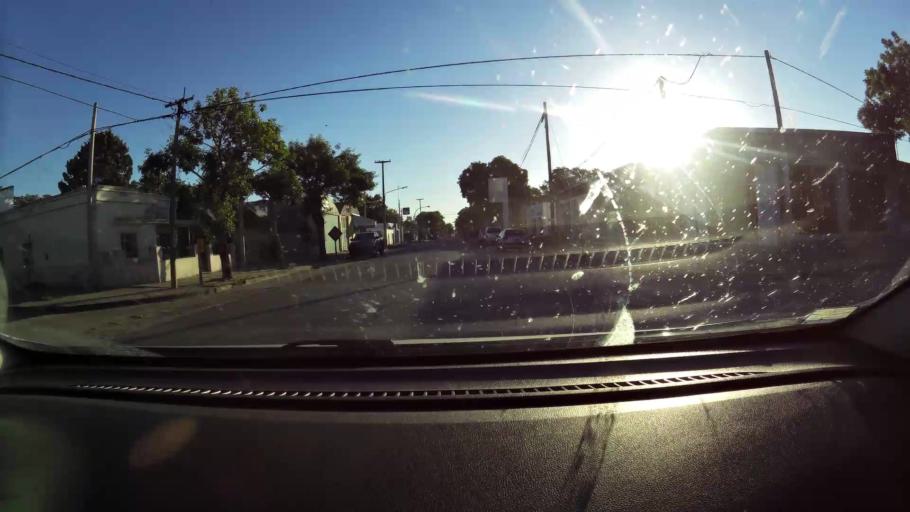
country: AR
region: Cordoba
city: Las Varillas
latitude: -31.8707
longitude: -62.7104
